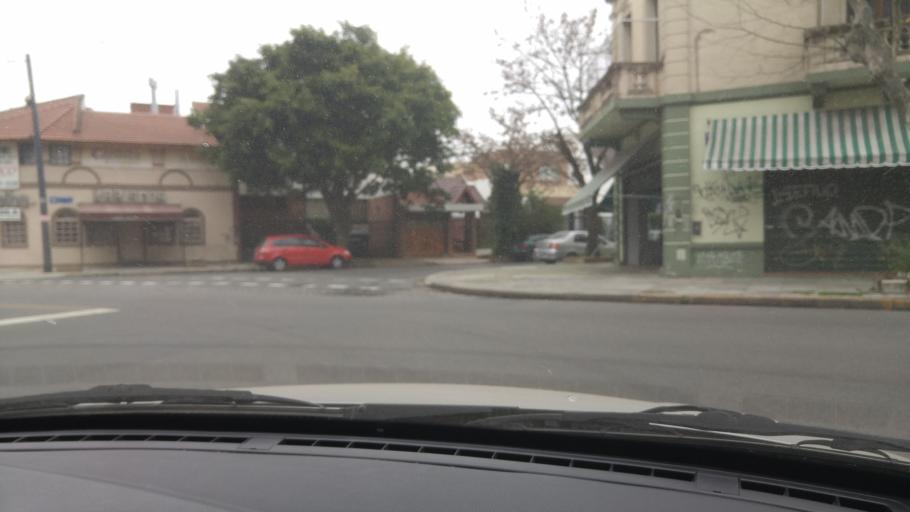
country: AR
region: Buenos Aires F.D.
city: Villa Santa Rita
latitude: -34.6325
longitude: -58.4910
